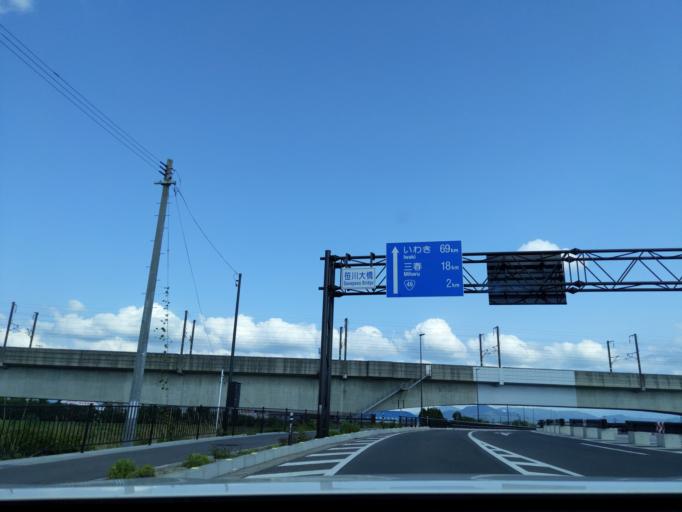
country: JP
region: Fukushima
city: Koriyama
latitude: 37.3599
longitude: 140.3742
